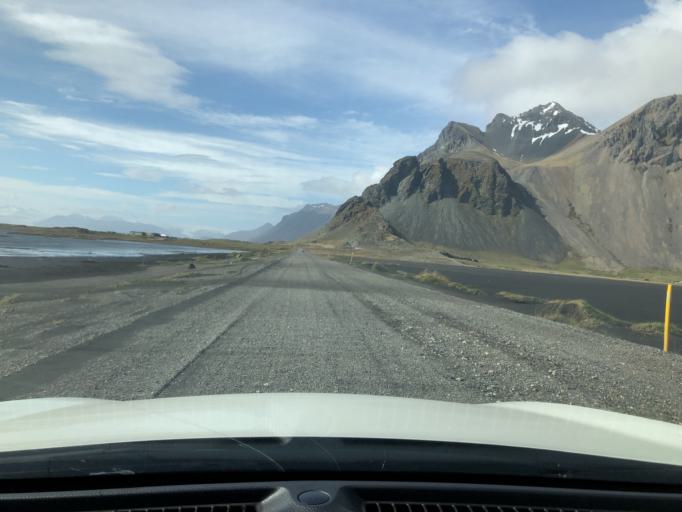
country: IS
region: East
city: Hoefn
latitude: 64.2487
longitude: -14.9815
